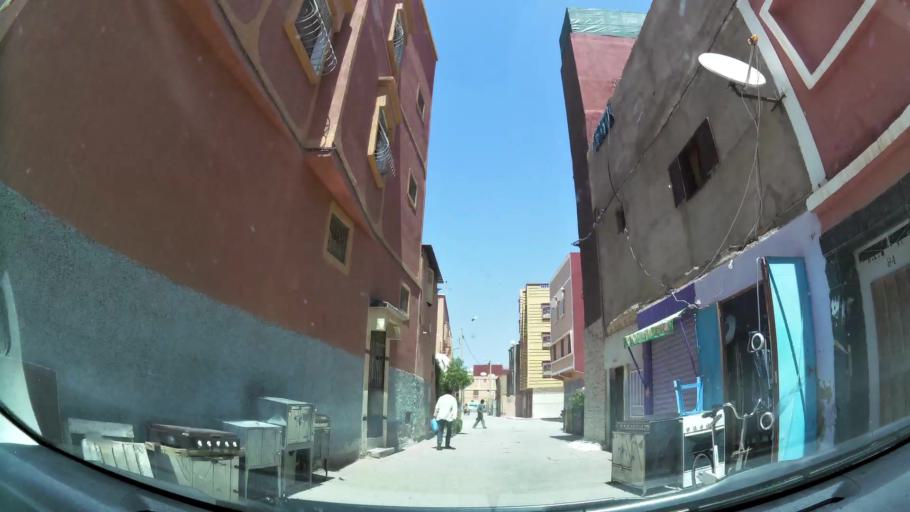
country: MA
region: Souss-Massa-Draa
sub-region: Inezgane-Ait Mellou
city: Inezgane
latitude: 30.3433
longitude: -9.4960
